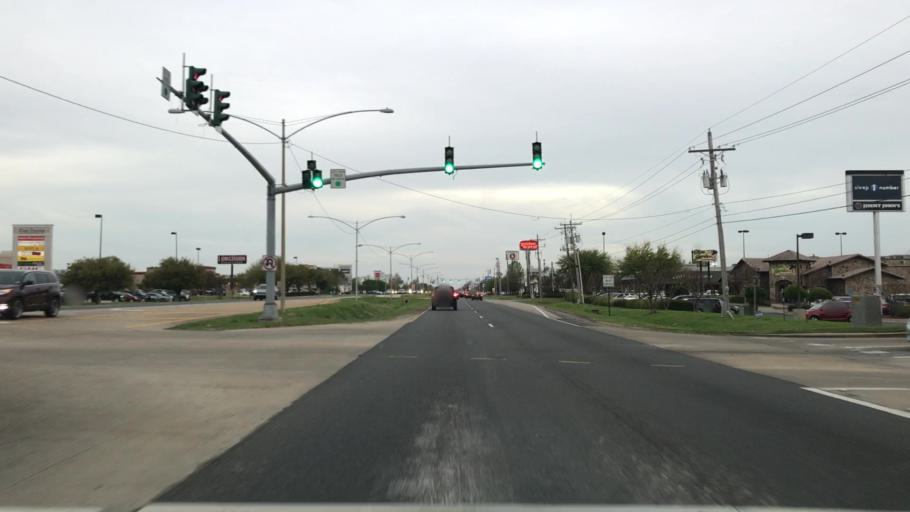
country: US
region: Louisiana
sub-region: Bossier Parish
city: Bossier City
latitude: 32.4414
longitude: -93.7176
